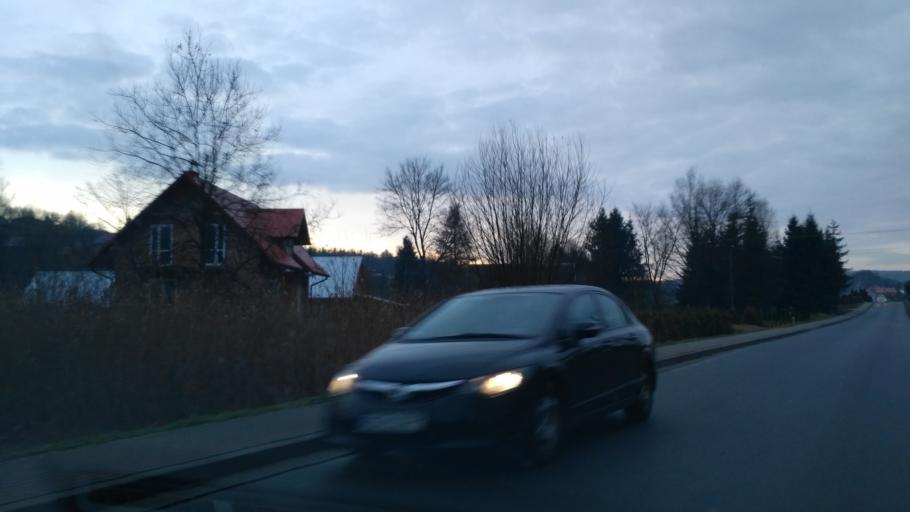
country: PL
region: Subcarpathian Voivodeship
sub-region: Powiat strzyzowski
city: Konieczkowa
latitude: 49.8483
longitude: 21.9166
